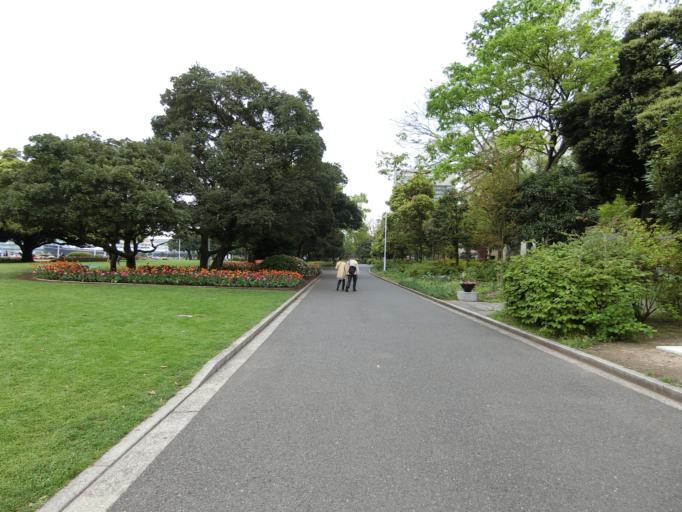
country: JP
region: Kanagawa
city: Yokohama
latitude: 35.4472
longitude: 139.6469
